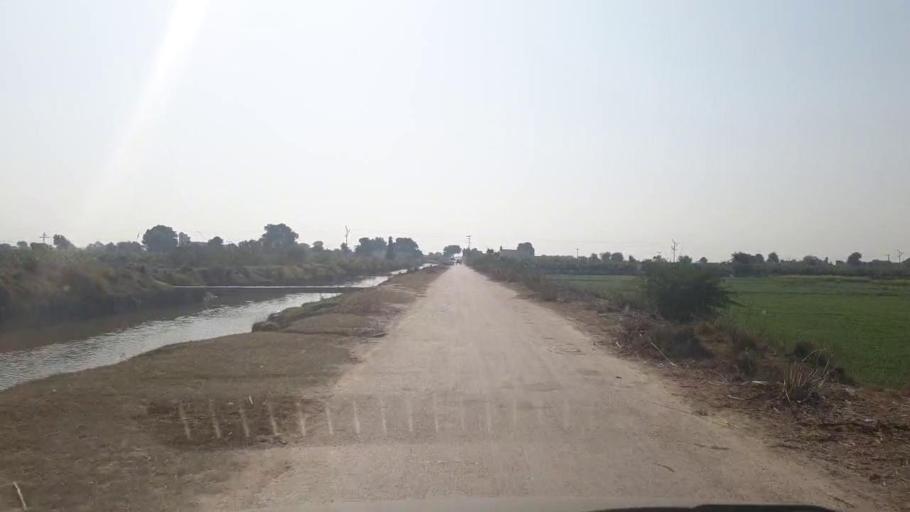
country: PK
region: Sindh
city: Tando Adam
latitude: 25.7413
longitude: 68.6196
